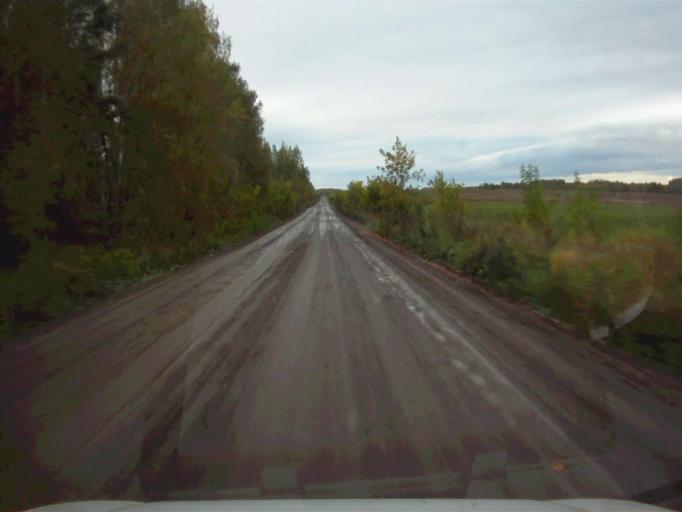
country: RU
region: Sverdlovsk
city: Mikhaylovsk
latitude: 56.1582
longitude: 59.2541
